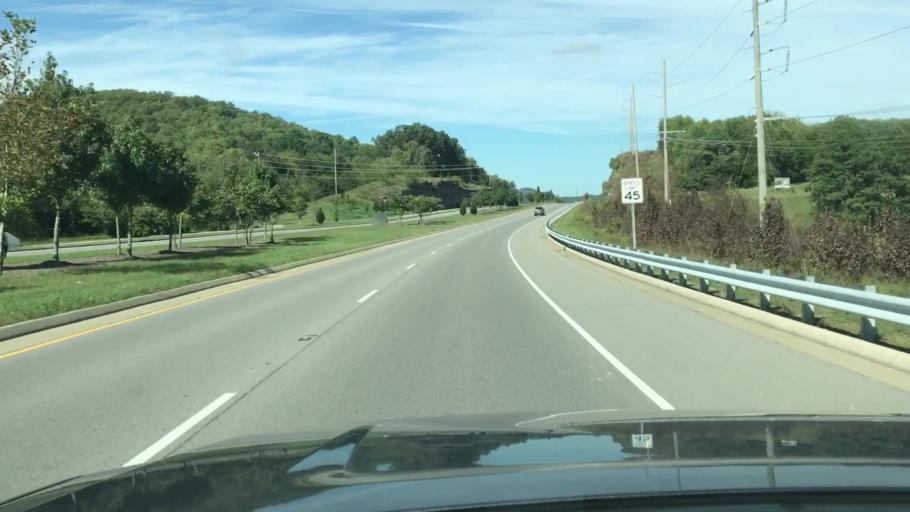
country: US
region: Tennessee
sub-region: Williamson County
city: Franklin
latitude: 35.9314
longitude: -86.8414
